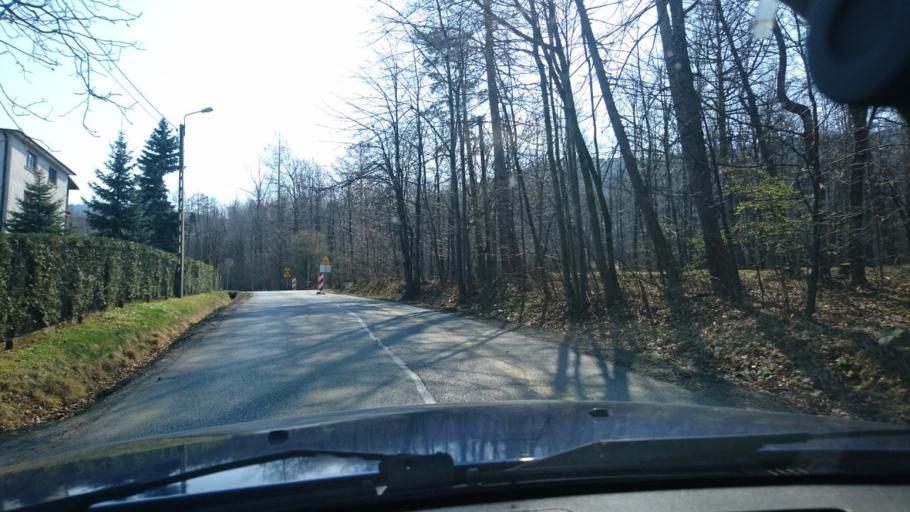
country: PL
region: Silesian Voivodeship
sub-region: Powiat bielski
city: Kozy
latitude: 49.8191
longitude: 19.1125
